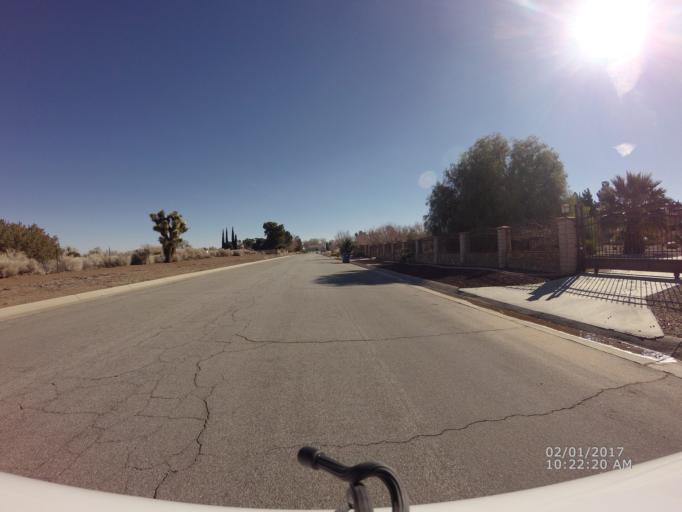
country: US
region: California
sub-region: Los Angeles County
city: Palmdale
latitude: 34.5458
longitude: -118.1179
